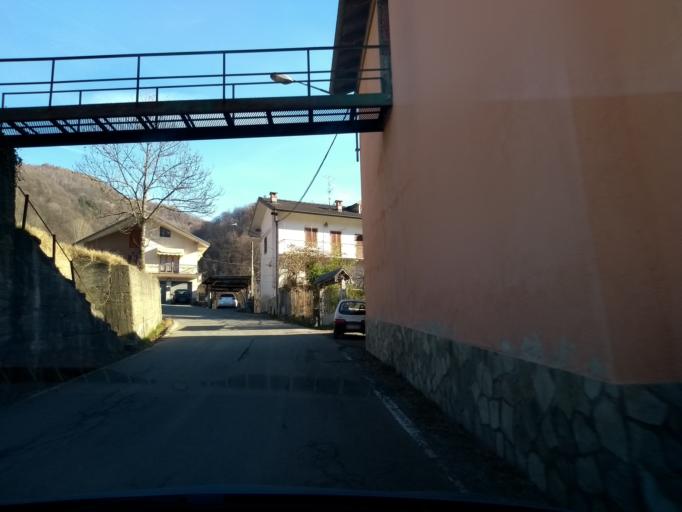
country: IT
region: Piedmont
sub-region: Provincia di Torino
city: Pessinetto
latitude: 45.2864
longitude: 7.4186
